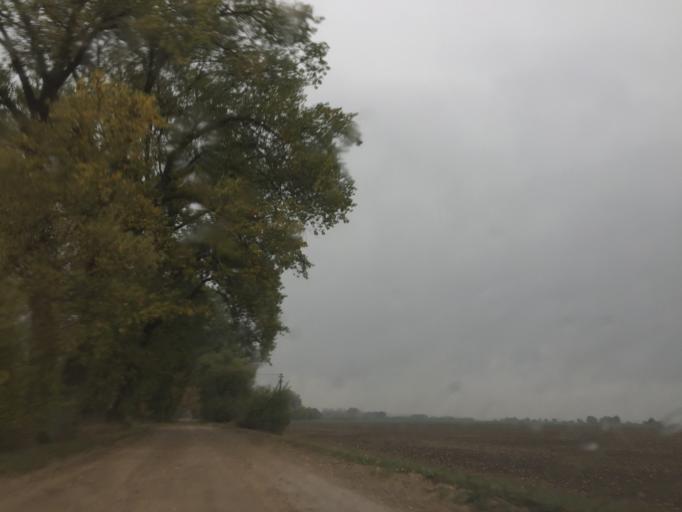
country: LV
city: Tireli
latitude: 56.7092
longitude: 23.4973
